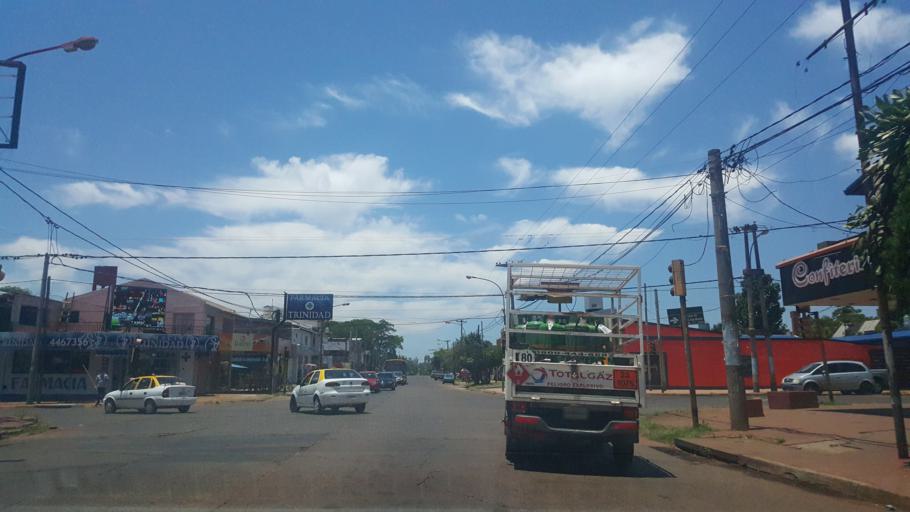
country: AR
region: Misiones
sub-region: Departamento de Capital
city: Posadas
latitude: -27.3689
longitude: -55.9172
